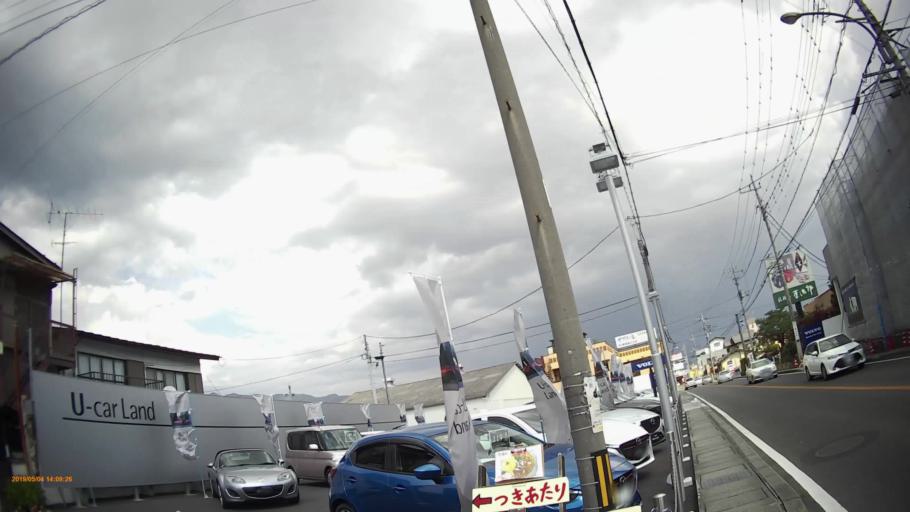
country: JP
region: Yamanashi
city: Kofu-shi
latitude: 35.6608
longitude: 138.5415
